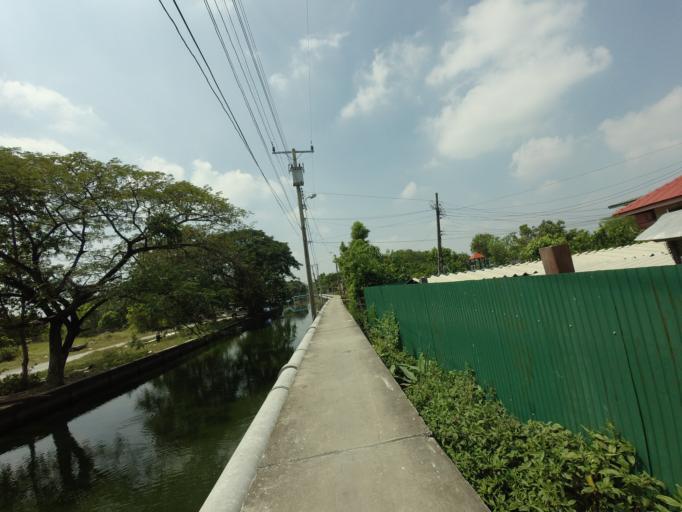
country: TH
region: Bangkok
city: Suan Luang
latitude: 13.7486
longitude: 100.6688
